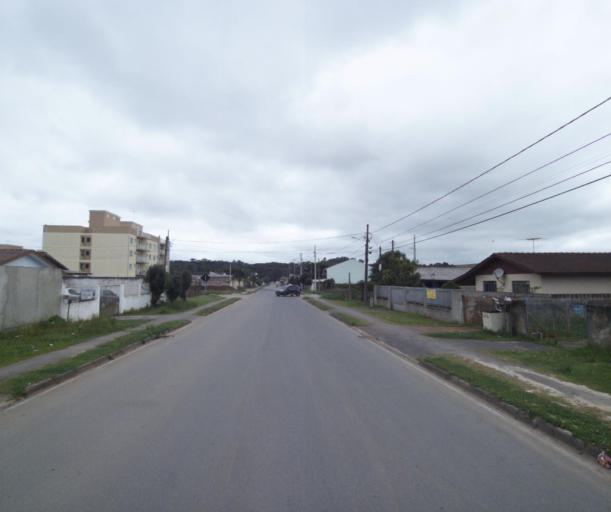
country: BR
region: Parana
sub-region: Quatro Barras
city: Quatro Barras
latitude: -25.3605
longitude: -49.0959
